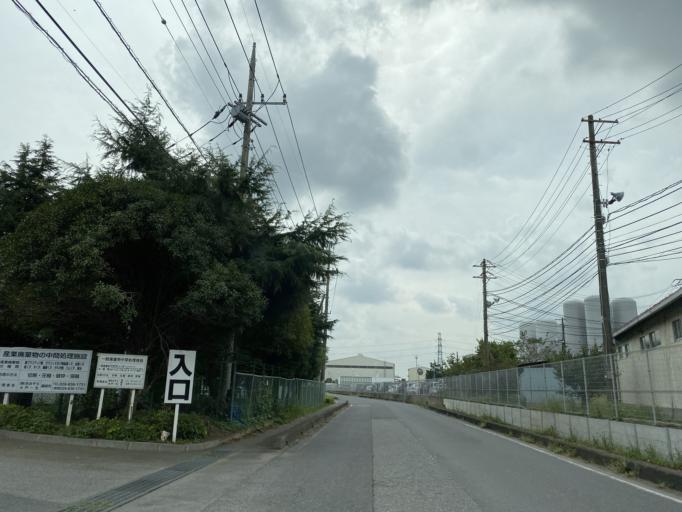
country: JP
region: Ibaraki
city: Mitsukaido
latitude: 36.0239
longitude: 140.0490
